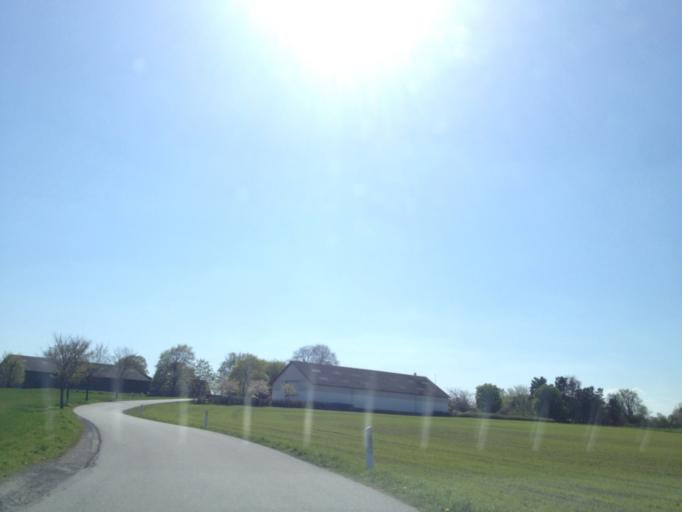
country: DK
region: Zealand
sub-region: Roskilde Kommune
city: Viby
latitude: 55.5151
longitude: 12.0108
